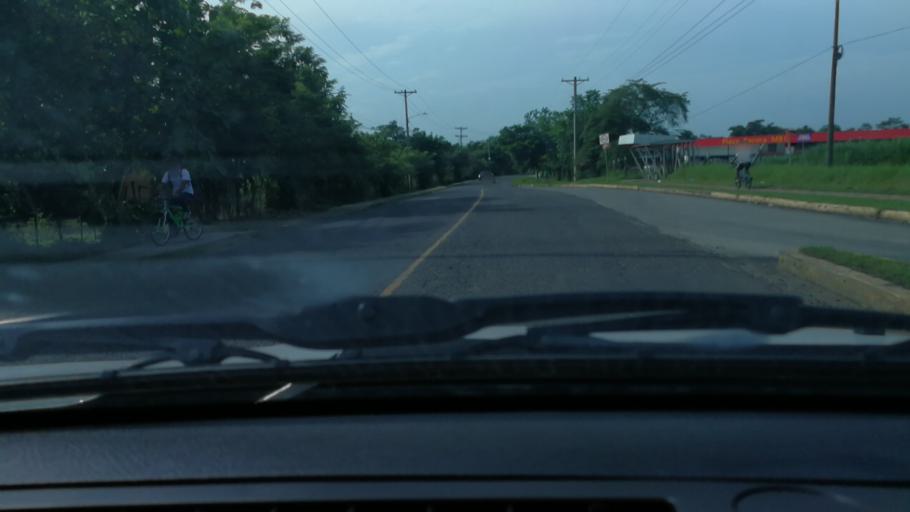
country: PA
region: Panama
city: Pacora
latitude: 9.0890
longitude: -79.2883
